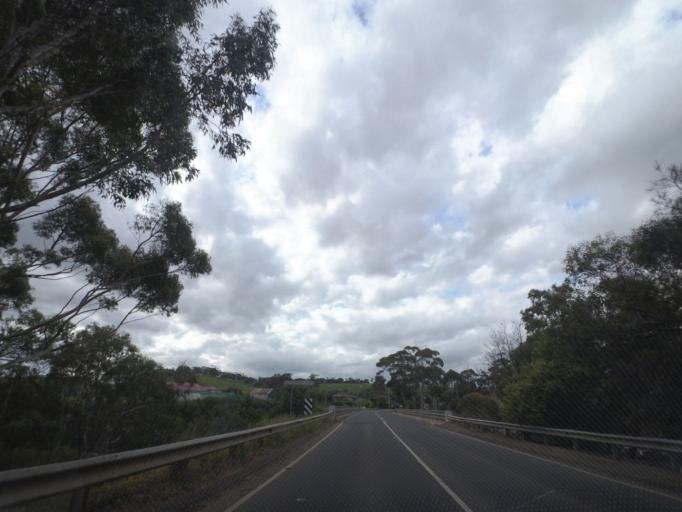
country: AU
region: Victoria
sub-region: Brimbank
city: Keilor
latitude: -37.7049
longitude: 144.8324
